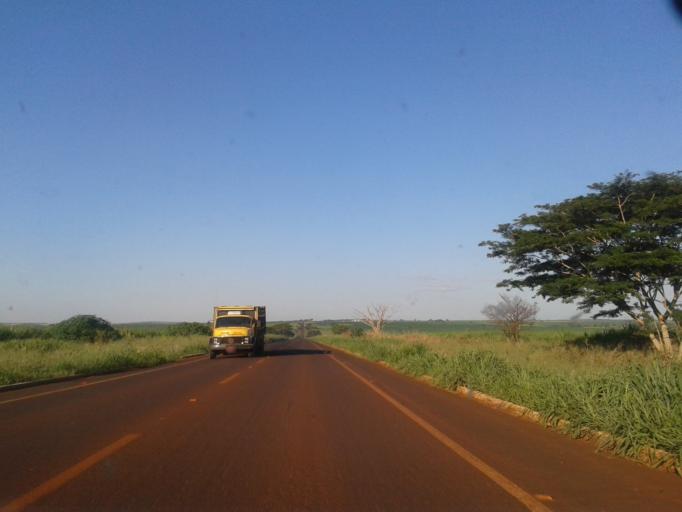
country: BR
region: Minas Gerais
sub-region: Capinopolis
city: Capinopolis
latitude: -18.7045
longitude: -49.6812
